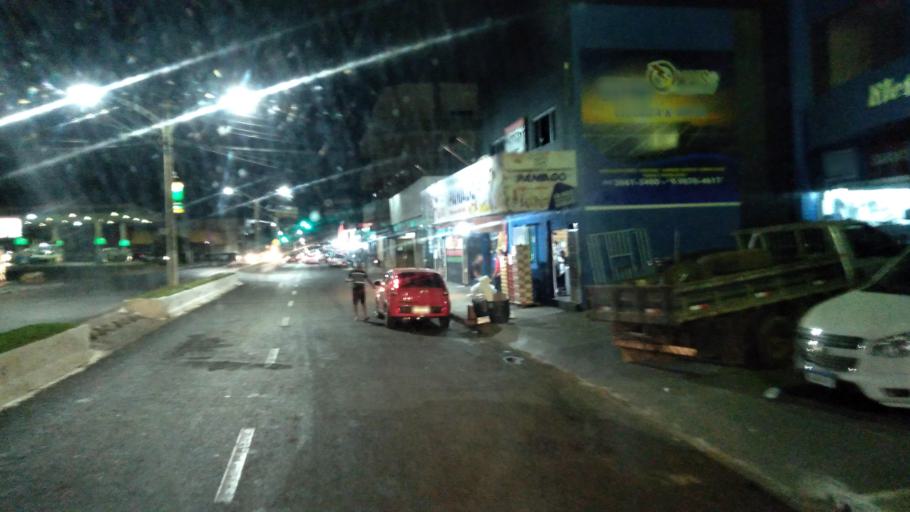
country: BR
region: Goias
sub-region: Mineiros
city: Mineiros
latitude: -17.5632
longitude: -52.5517
